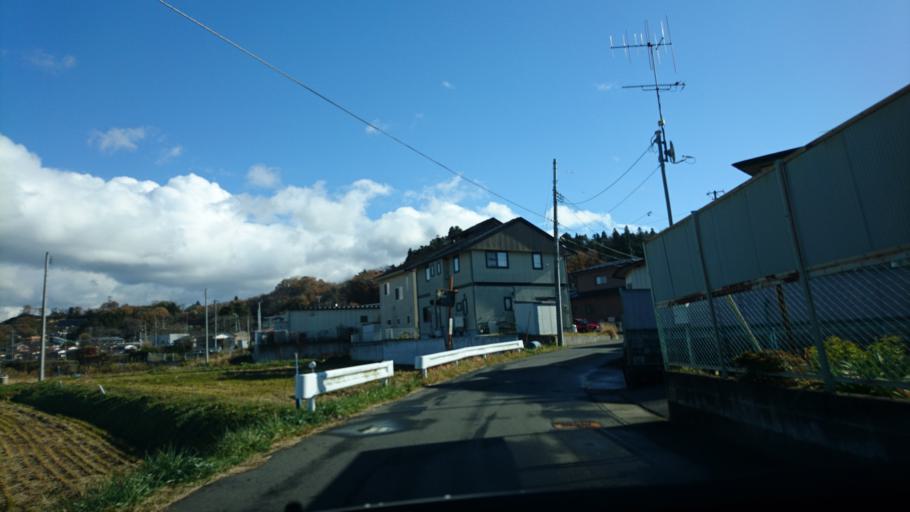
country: JP
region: Iwate
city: Ichinoseki
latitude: 38.9212
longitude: 141.1168
